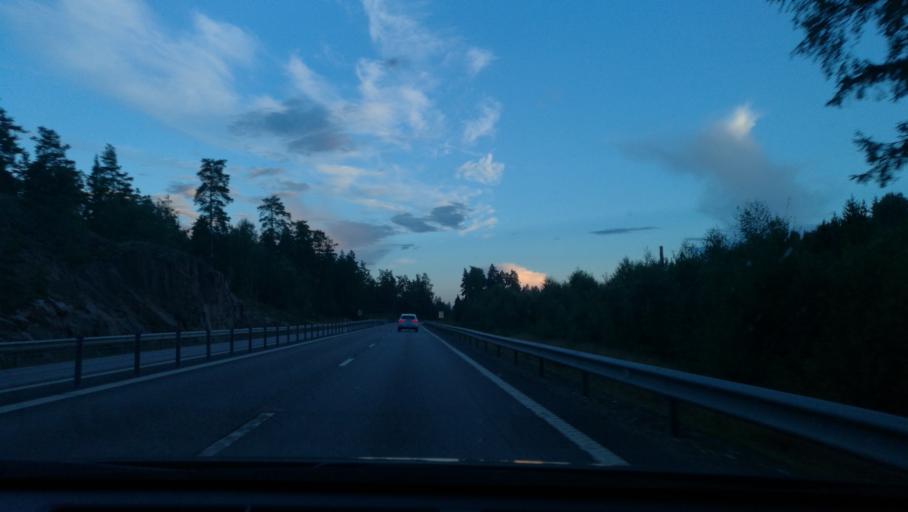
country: SE
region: Soedermanland
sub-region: Katrineholms Kommun
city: Katrineholm
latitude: 58.8360
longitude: 16.1958
